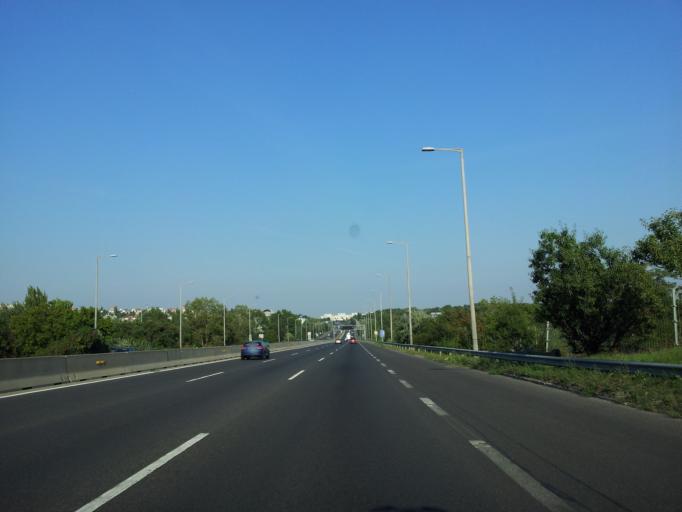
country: HU
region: Pest
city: Budaors
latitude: 47.4591
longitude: 18.9897
